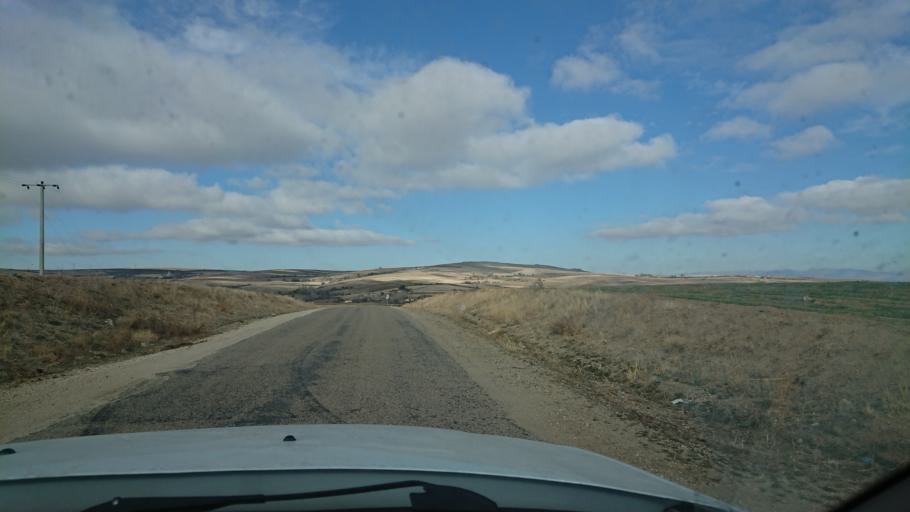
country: TR
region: Aksaray
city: Agacoren
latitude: 38.8169
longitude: 33.9810
